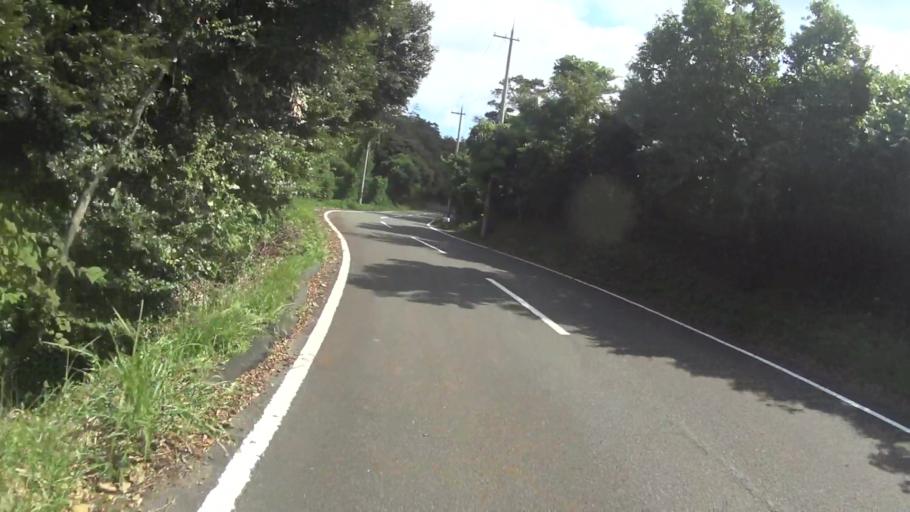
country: JP
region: Kyoto
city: Miyazu
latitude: 35.7470
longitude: 135.1707
